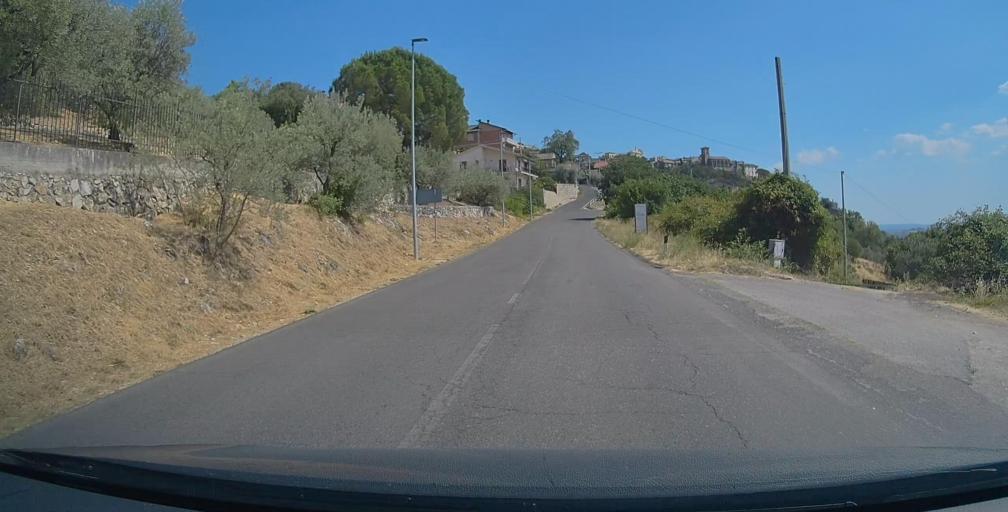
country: IT
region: Umbria
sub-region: Provincia di Terni
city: Calvi dell'Umbria
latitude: 42.4064
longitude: 12.5652
